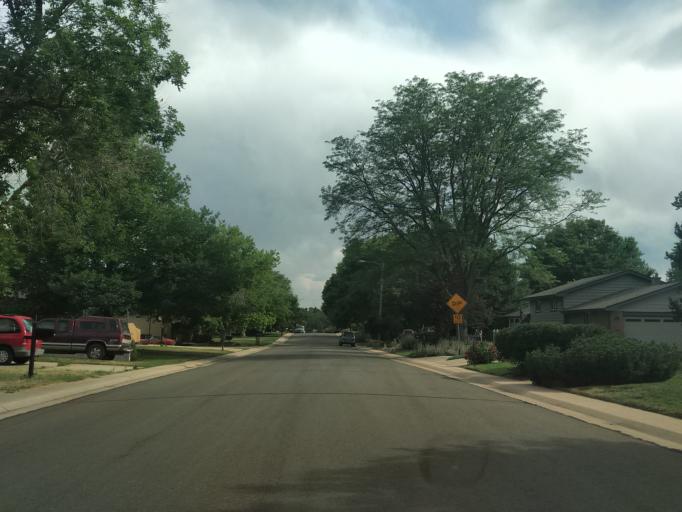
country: US
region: Colorado
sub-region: Jefferson County
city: Lakewood
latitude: 39.7029
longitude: -105.0946
